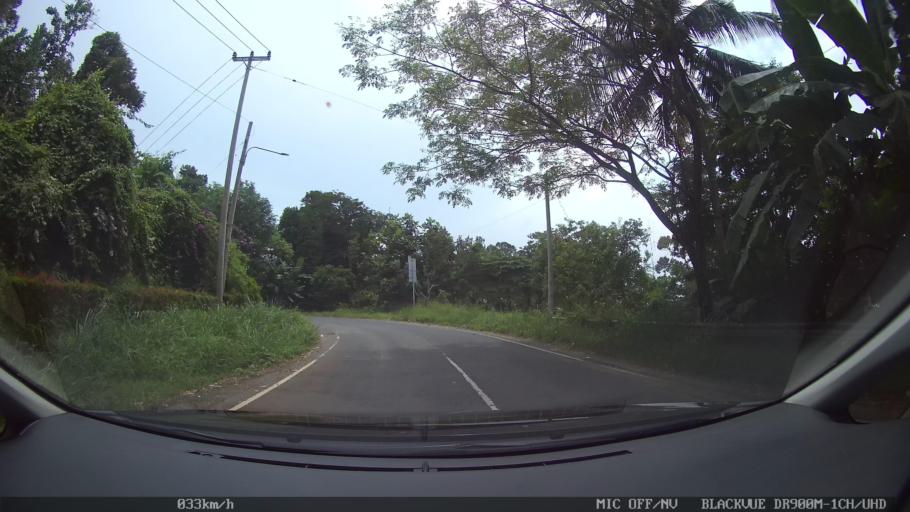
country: ID
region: Lampung
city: Bandarlampung
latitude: -5.4234
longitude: 105.2361
